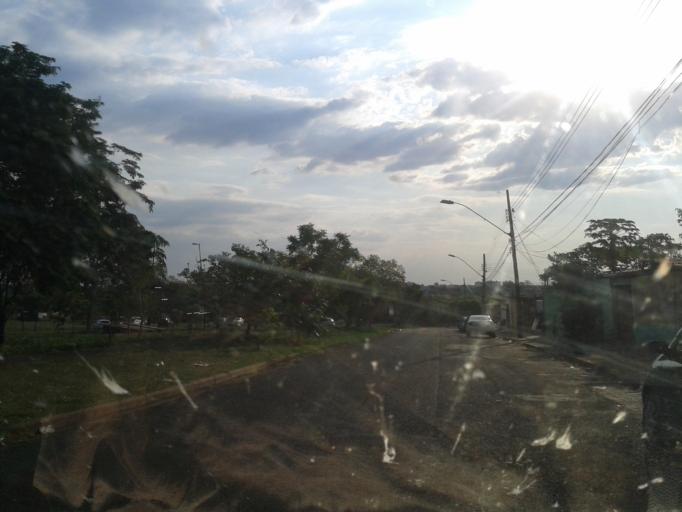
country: BR
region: Minas Gerais
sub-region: Uberlandia
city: Uberlandia
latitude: -18.9417
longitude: -48.3185
